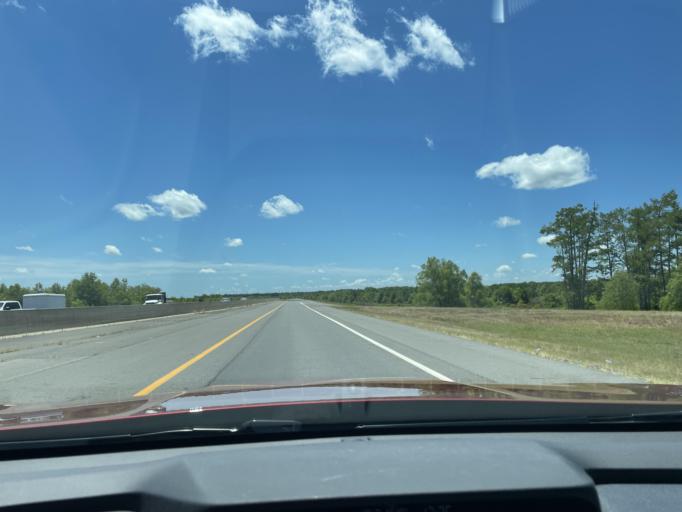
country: US
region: Arkansas
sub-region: Jefferson County
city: Pine Bluff
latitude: 34.1690
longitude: -91.9860
